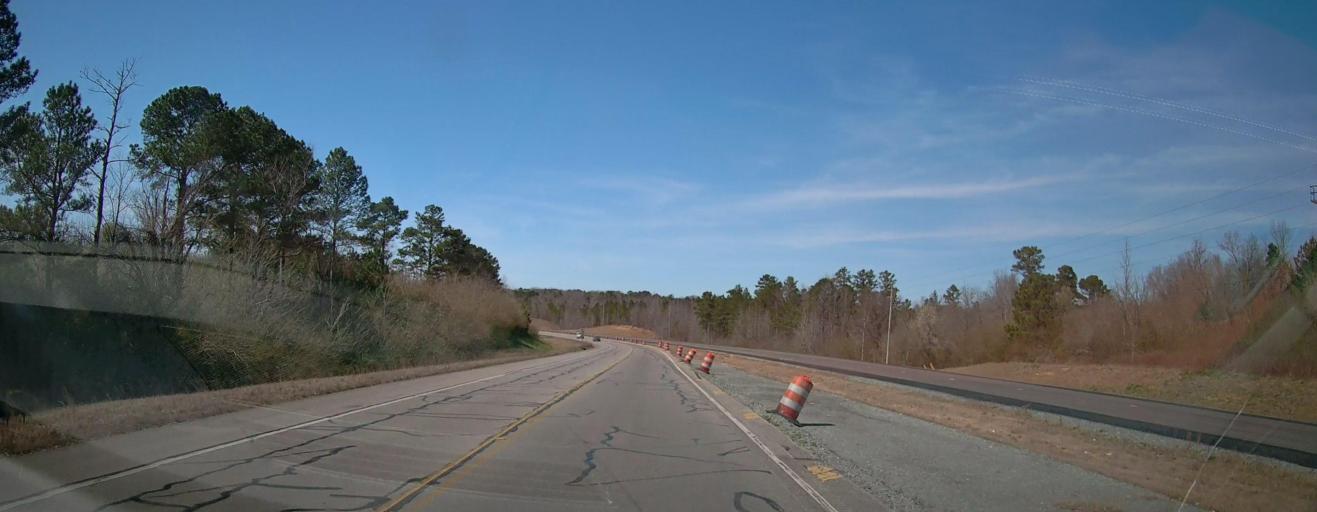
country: US
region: Alabama
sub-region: Cullman County
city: Cullman
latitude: 34.1957
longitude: -86.7893
